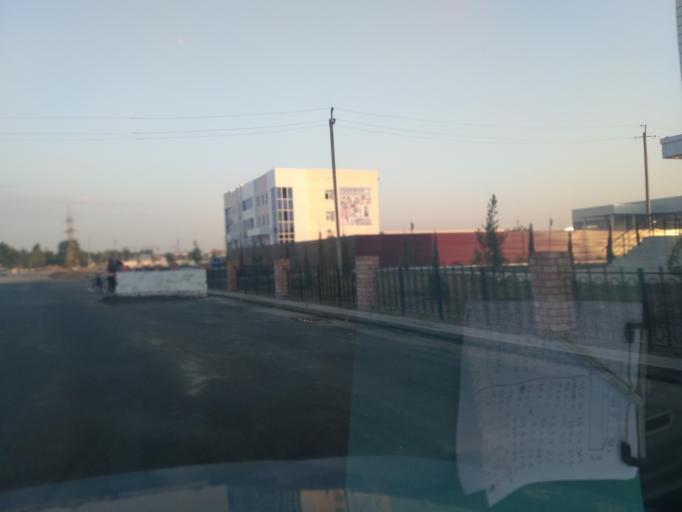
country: UZ
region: Sirdaryo
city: Guliston
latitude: 40.5061
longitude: 68.7677
